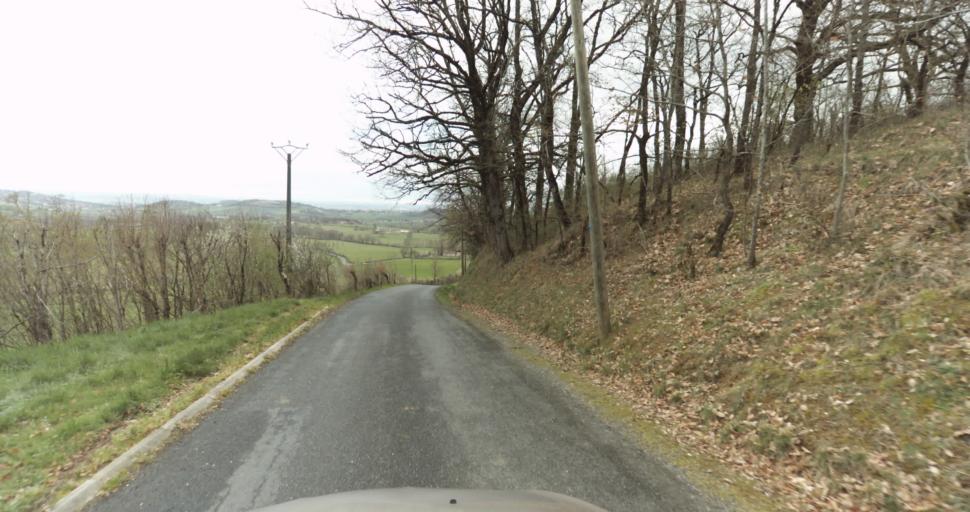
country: FR
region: Midi-Pyrenees
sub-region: Departement du Tarn
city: Frejairolles
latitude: 43.8674
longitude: 2.2059
